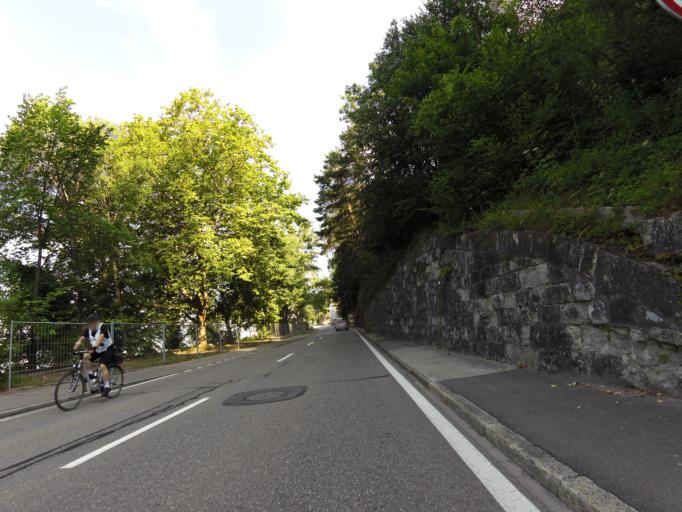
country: CH
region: Zug
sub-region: Zug
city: Walchwil
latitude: 47.1131
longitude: 8.5011
